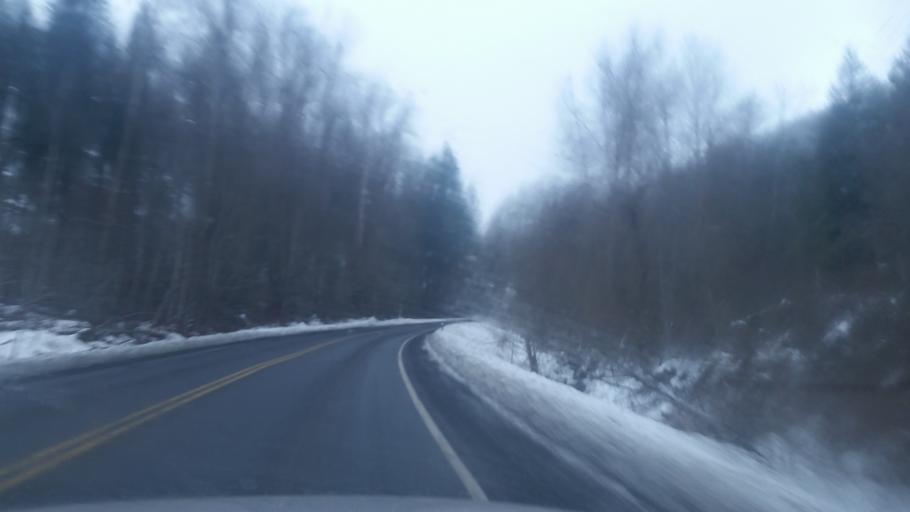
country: US
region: Washington
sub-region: Lincoln County
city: Davenport
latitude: 47.7631
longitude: -117.8907
